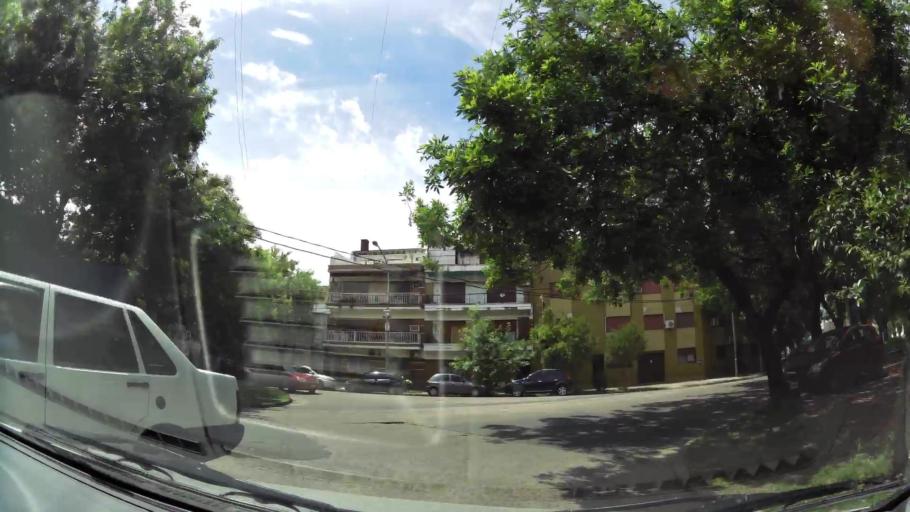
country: AR
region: Buenos Aires
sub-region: Partido de Lanus
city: Lanus
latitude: -34.6653
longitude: -58.4155
